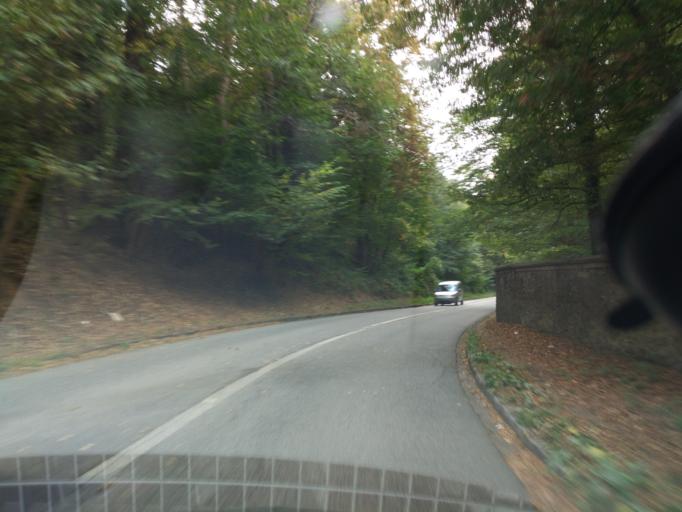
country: FR
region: Ile-de-France
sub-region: Departement des Yvelines
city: Saint-Remy-les-Chevreuse
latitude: 48.6920
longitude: 2.0675
